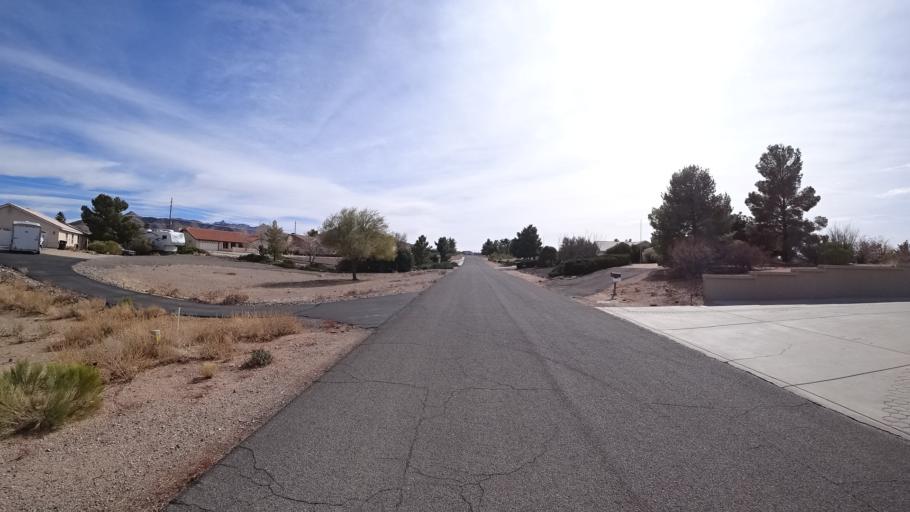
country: US
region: Arizona
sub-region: Mohave County
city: Kingman
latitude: 35.1939
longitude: -113.9880
